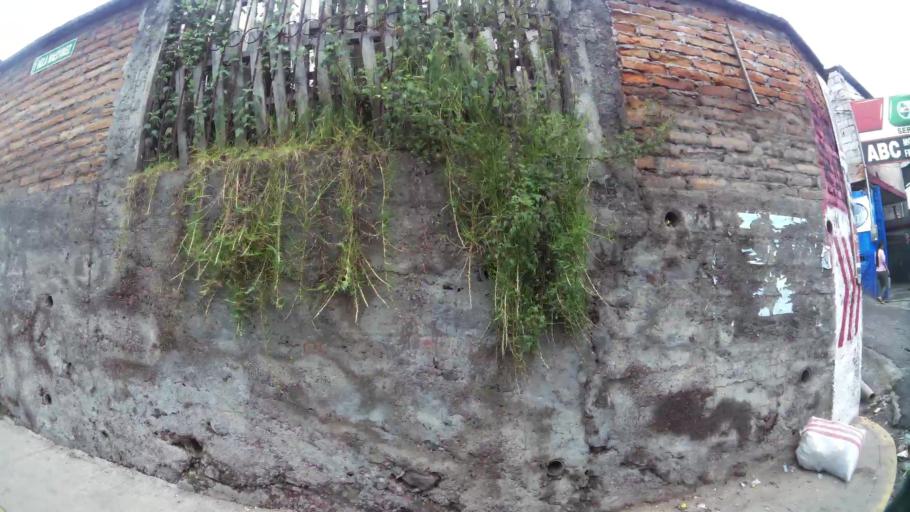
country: EC
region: Pichincha
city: Quito
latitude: -0.2631
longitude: -78.4872
